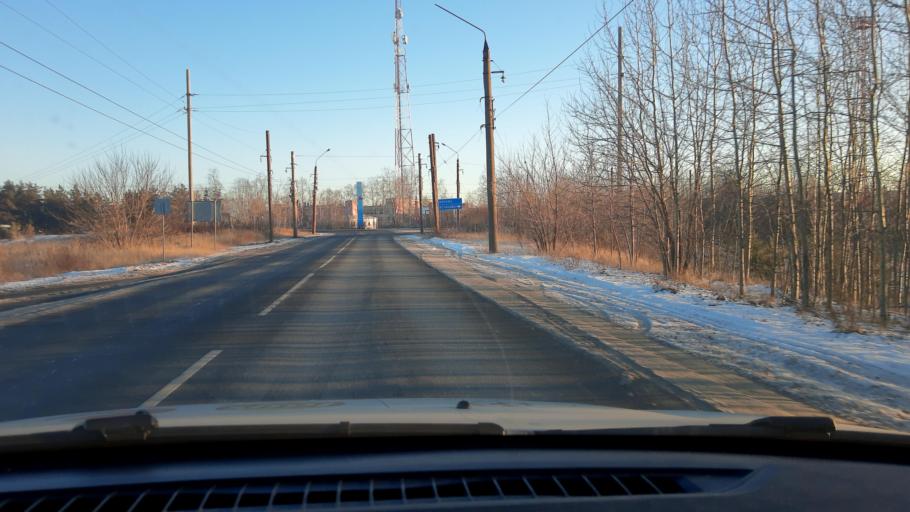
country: RU
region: Nizjnij Novgorod
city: Babino
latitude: 56.2906
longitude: 43.5969
